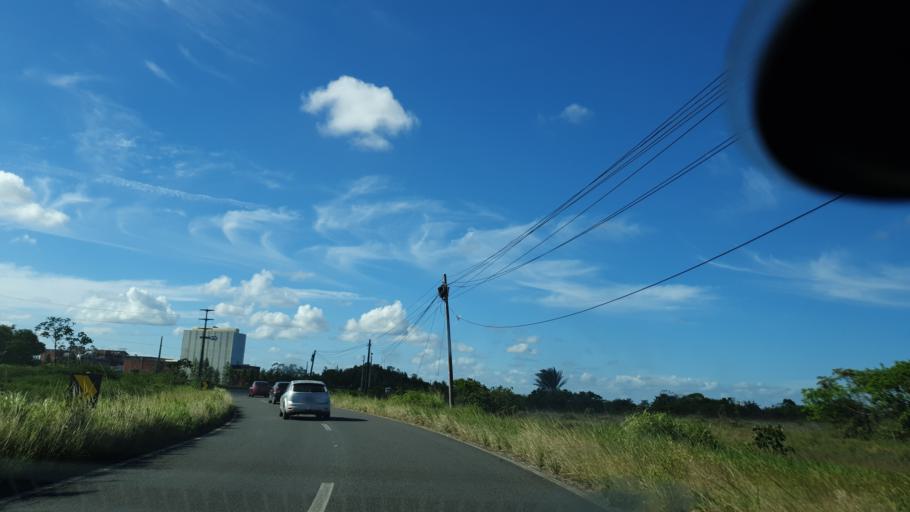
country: BR
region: Bahia
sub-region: Camacari
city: Camacari
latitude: -12.6673
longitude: -38.3003
